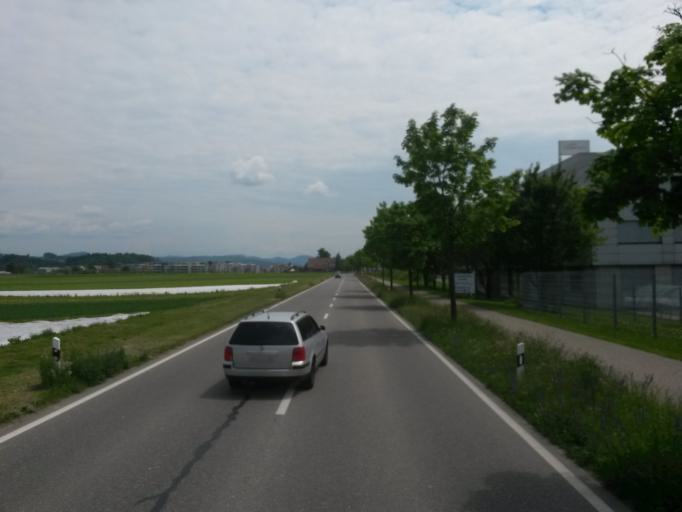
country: CH
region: Zurich
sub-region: Bezirk Pfaeffikon
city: Fehraltorf
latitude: 47.3950
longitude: 8.7405
